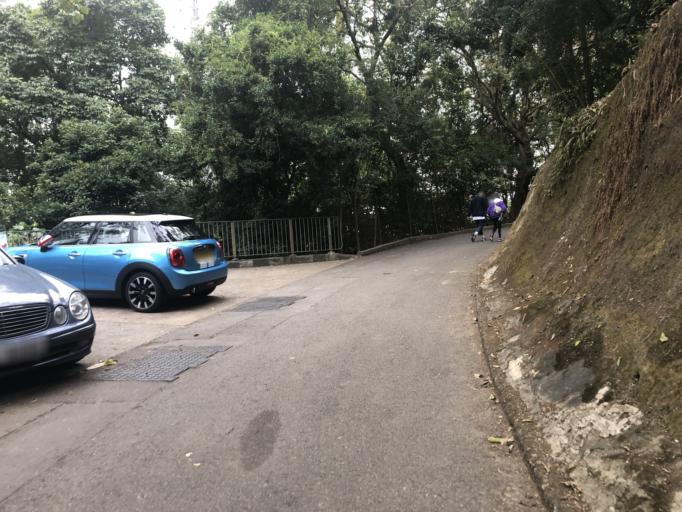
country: HK
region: Wanchai
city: Wan Chai
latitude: 22.2831
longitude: 114.2121
